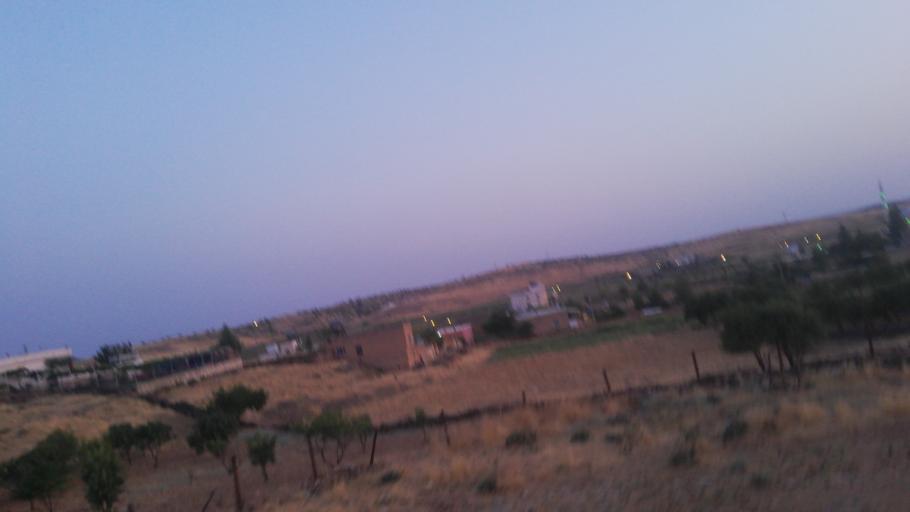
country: TR
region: Mardin
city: Kindirip
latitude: 37.4483
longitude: 41.2244
